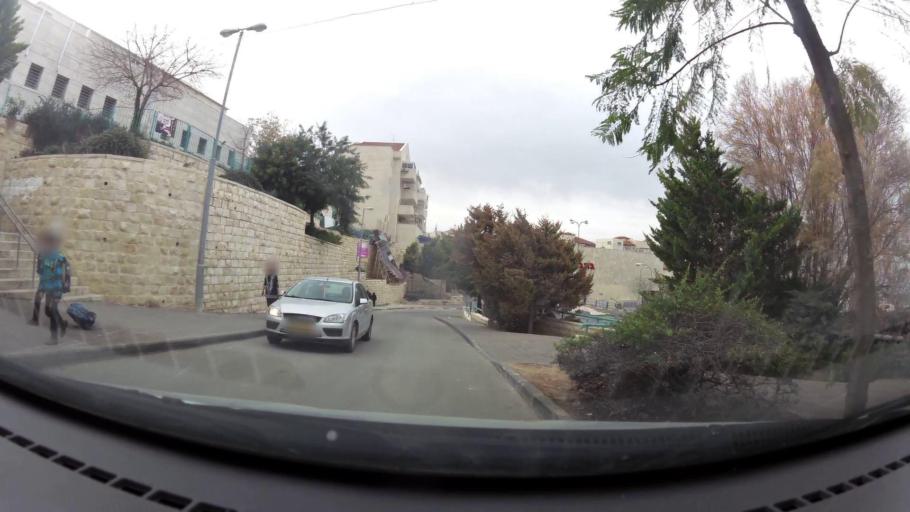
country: IL
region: Jerusalem
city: Bet Shemesh
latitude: 31.7143
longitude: 34.9948
